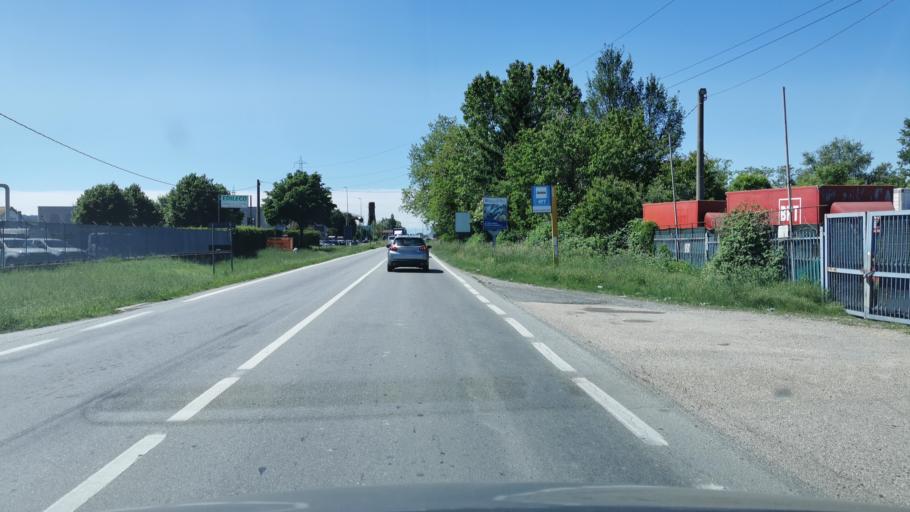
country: IT
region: Piedmont
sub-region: Provincia di Torino
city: Settimo Torinese
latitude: 45.1518
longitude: 7.7482
